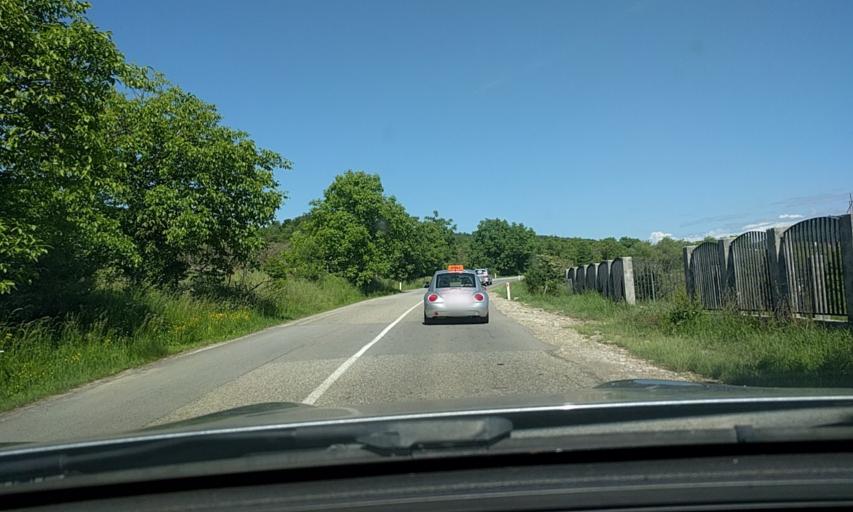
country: RO
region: Bistrita-Nasaud
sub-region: Municipiul Bistrita
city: Unirea
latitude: 47.1724
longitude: 24.4954
